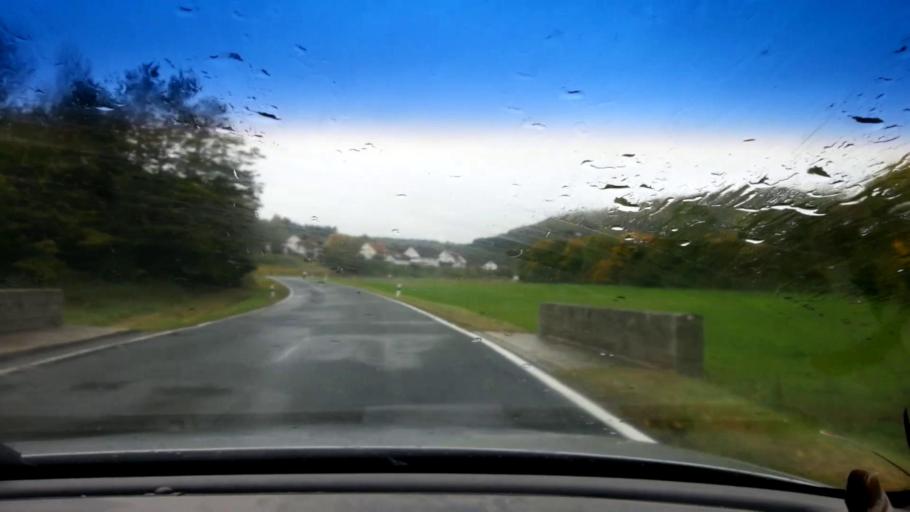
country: DE
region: Bavaria
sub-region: Upper Franconia
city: Heiligenstadt
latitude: 49.8769
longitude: 11.1671
